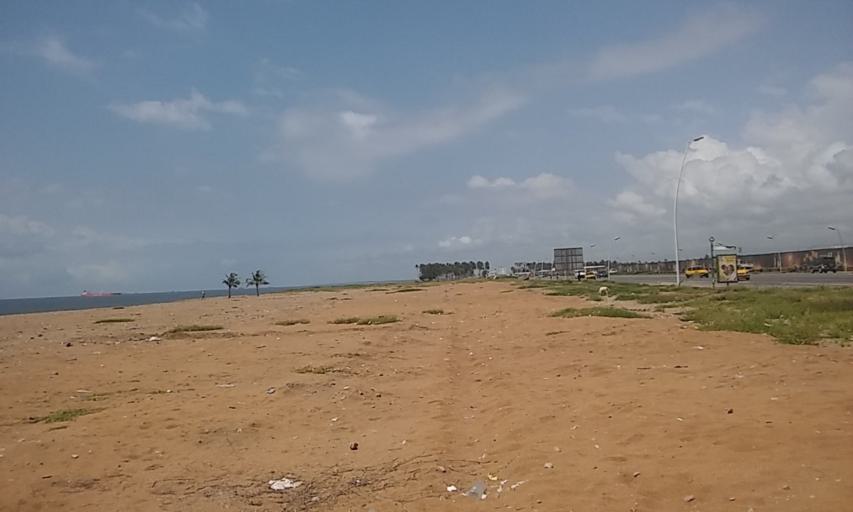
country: CI
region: Lagunes
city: Abidjan
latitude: 5.2443
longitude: -3.9295
